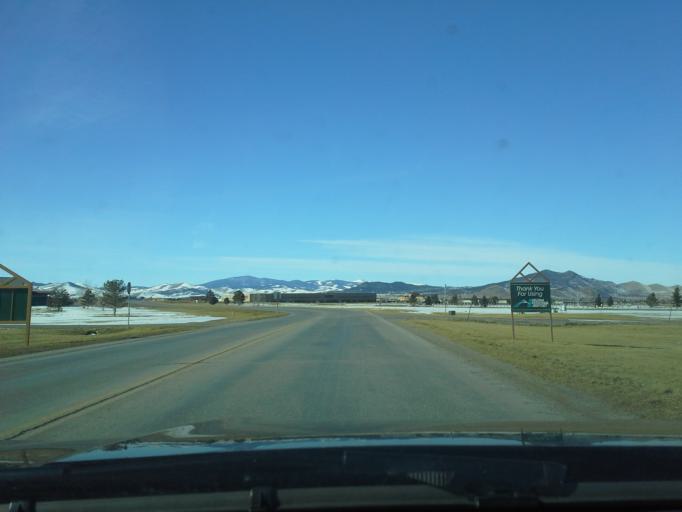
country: US
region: Montana
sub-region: Lewis and Clark County
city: Helena
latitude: 46.6126
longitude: -111.9942
